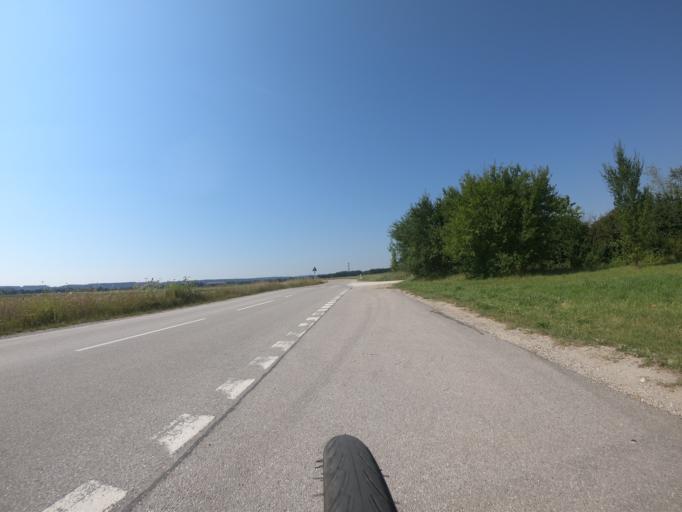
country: DE
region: Bavaria
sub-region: Upper Bavaria
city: Emmering
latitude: 48.2054
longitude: 11.2919
